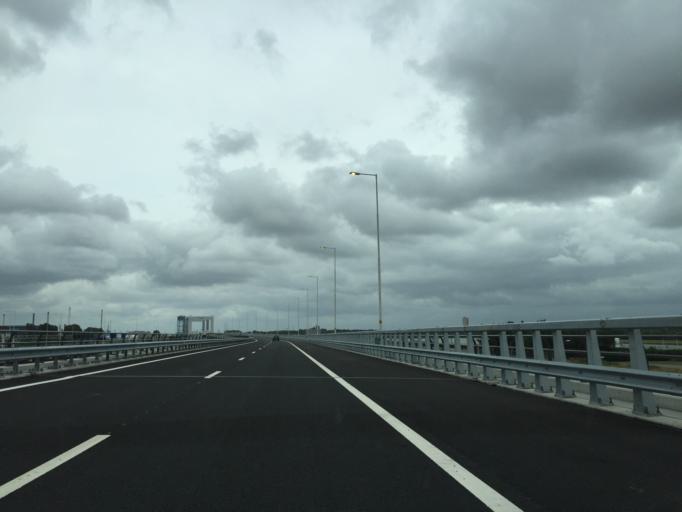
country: NL
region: South Holland
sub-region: Gemeente Spijkenisse
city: Spijkenisse
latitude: 51.8679
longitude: 4.3081
